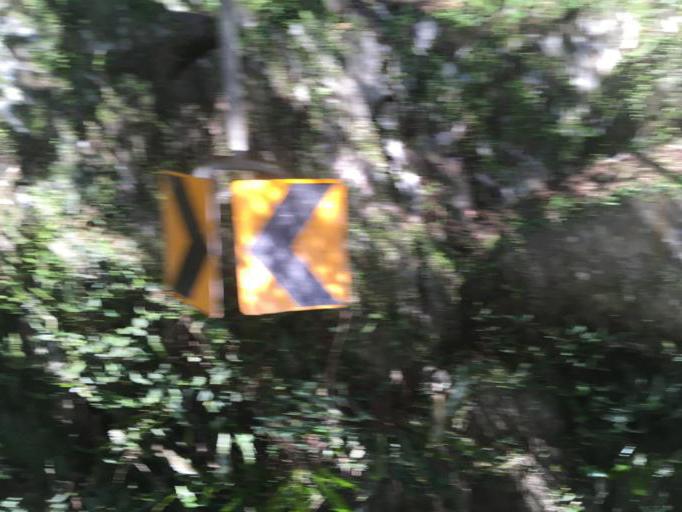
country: TW
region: Taiwan
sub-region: Yilan
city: Yilan
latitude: 24.7579
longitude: 121.6163
